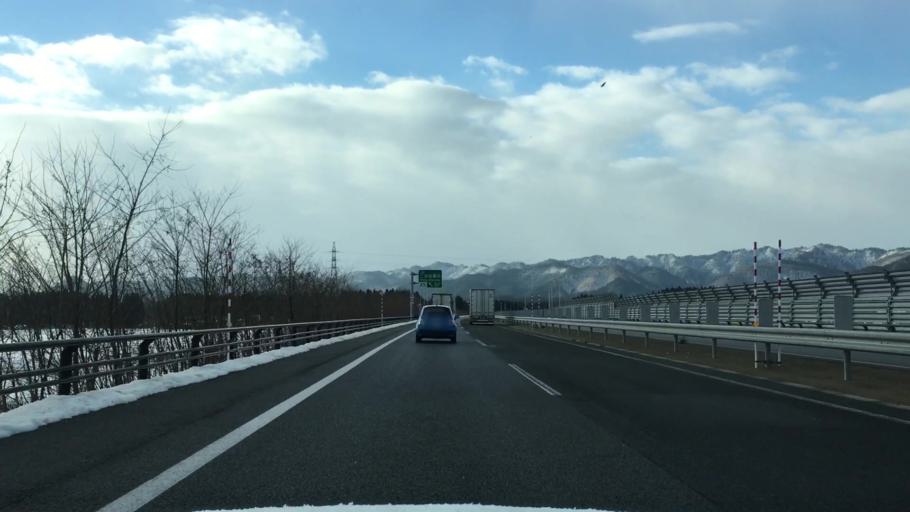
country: JP
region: Akita
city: Odate
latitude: 40.2546
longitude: 140.5194
